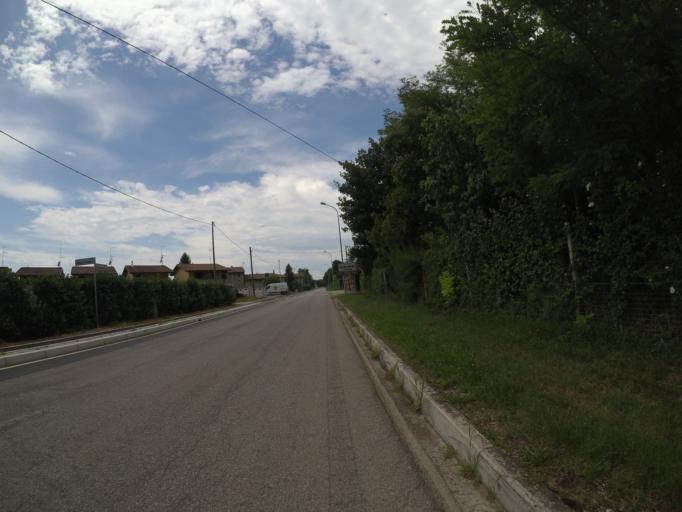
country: IT
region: Friuli Venezia Giulia
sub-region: Provincia di Udine
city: Castions di Strada
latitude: 45.9206
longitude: 13.1527
